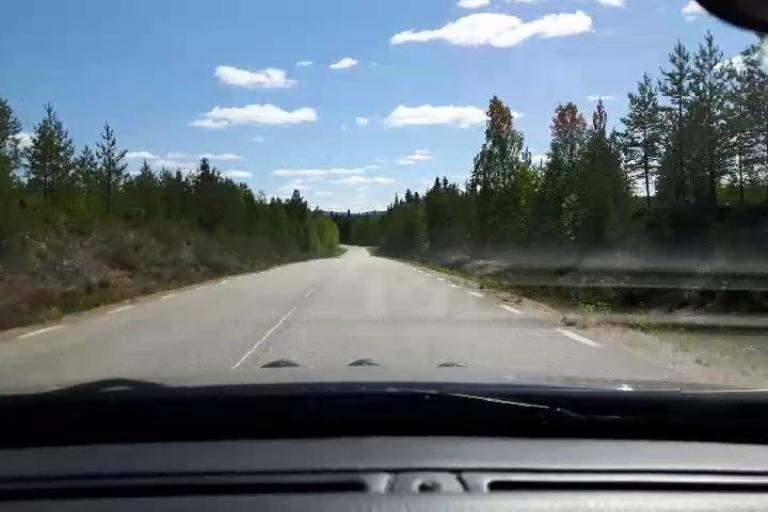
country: SE
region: Gaevleborg
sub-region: Ljusdals Kommun
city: Farila
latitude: 61.9991
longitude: 15.2415
